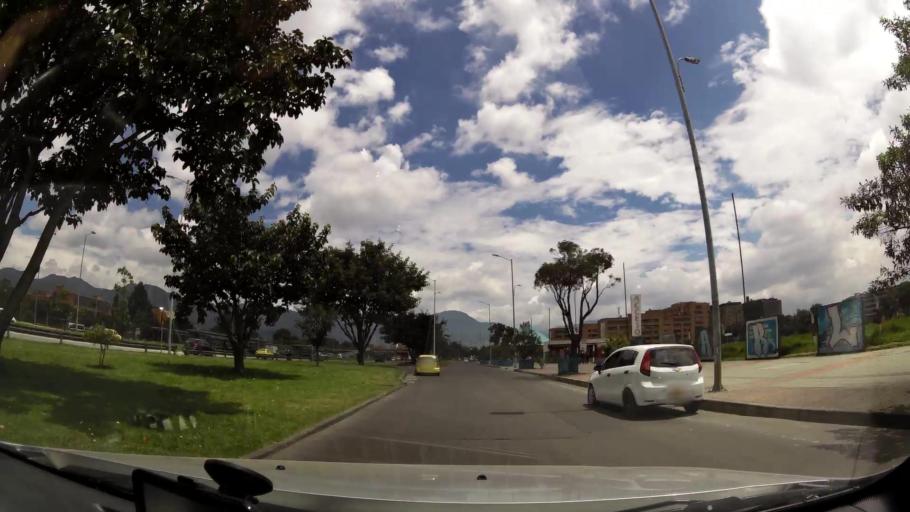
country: CO
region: Bogota D.C.
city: Bogota
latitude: 4.6436
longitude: -74.0977
